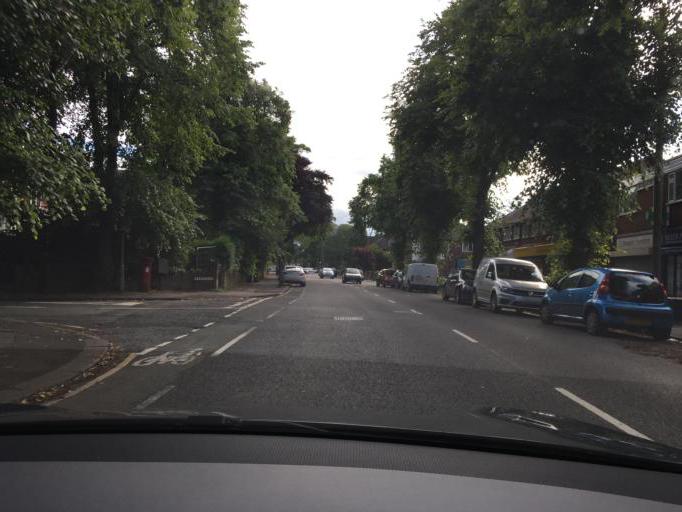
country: GB
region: England
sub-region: Trafford
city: Urmston
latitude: 53.4448
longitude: -2.3637
